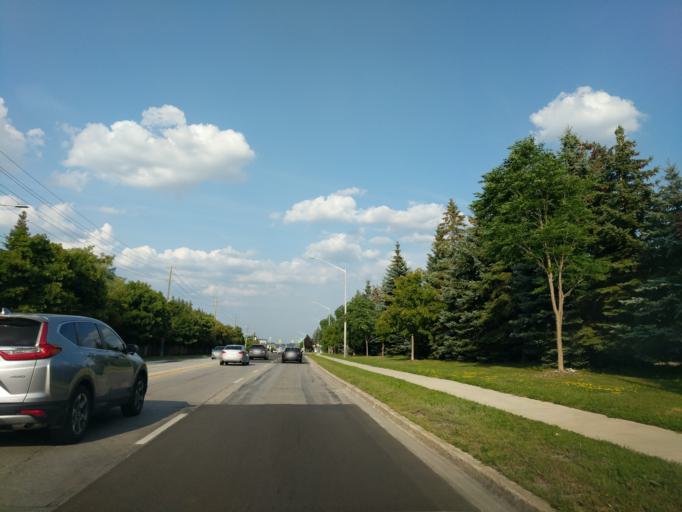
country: CA
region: Ontario
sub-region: York
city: Richmond Hill
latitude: 43.8597
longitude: -79.3988
